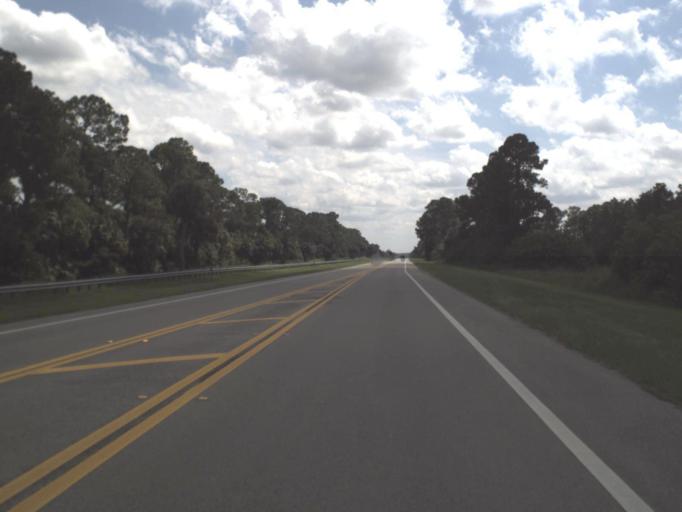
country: US
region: Florida
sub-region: Collier County
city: Immokalee
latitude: 26.4006
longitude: -81.3888
